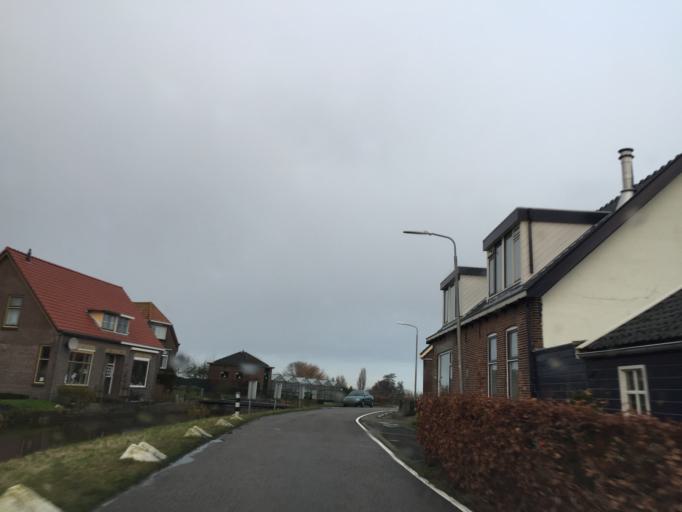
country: NL
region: South Holland
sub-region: Gemeente Pijnacker-Nootdorp
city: Pijnacker
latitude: 51.9876
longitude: 4.4241
